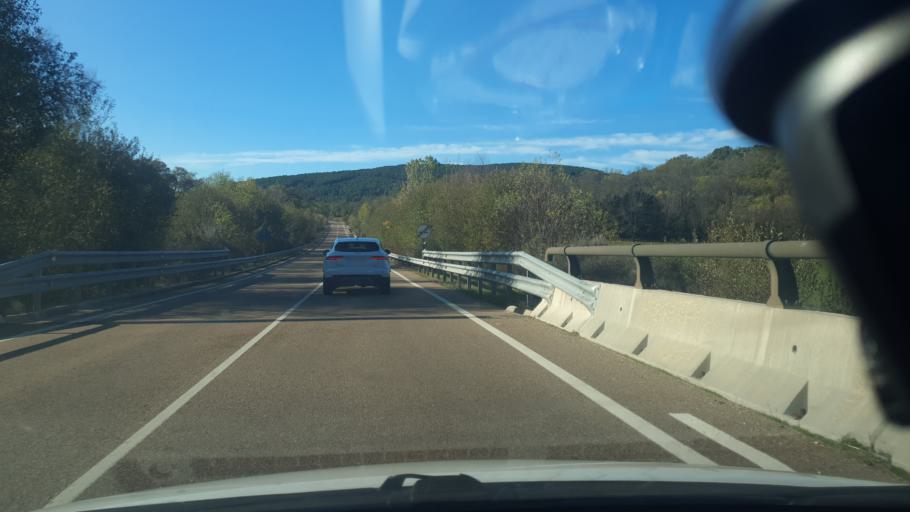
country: ES
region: Castille and Leon
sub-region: Provincia de Avila
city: Arenas de San Pedro
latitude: 40.1888
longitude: -5.0769
